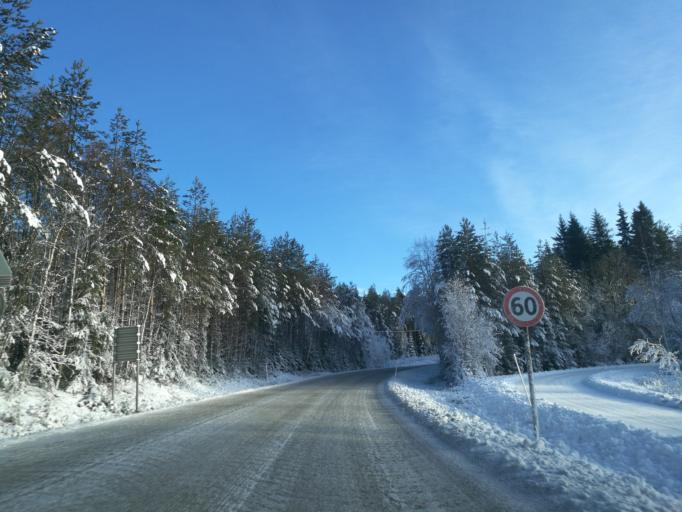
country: NO
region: Hedmark
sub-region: Grue
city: Kirkenaer
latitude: 60.4213
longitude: 12.4102
